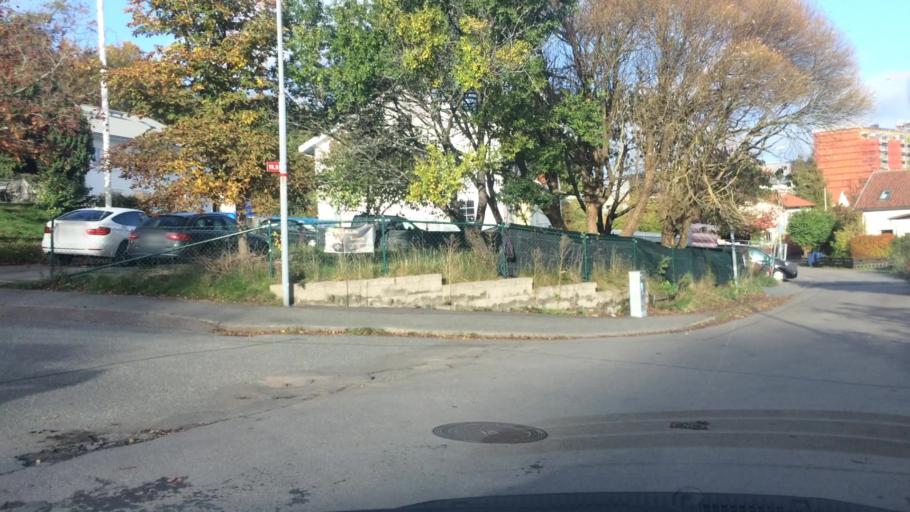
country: SE
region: Vaestra Goetaland
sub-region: Molndal
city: Moelndal
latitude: 57.6528
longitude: 12.0098
